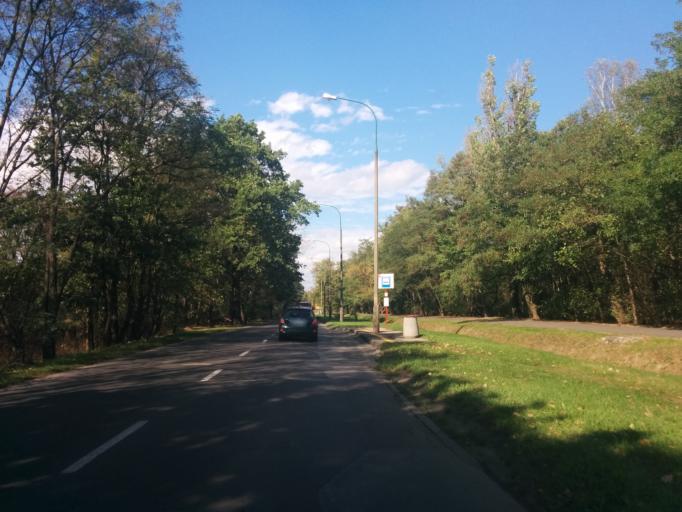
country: PL
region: Masovian Voivodeship
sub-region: Warszawa
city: Bialoleka
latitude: 52.3250
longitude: 20.9931
